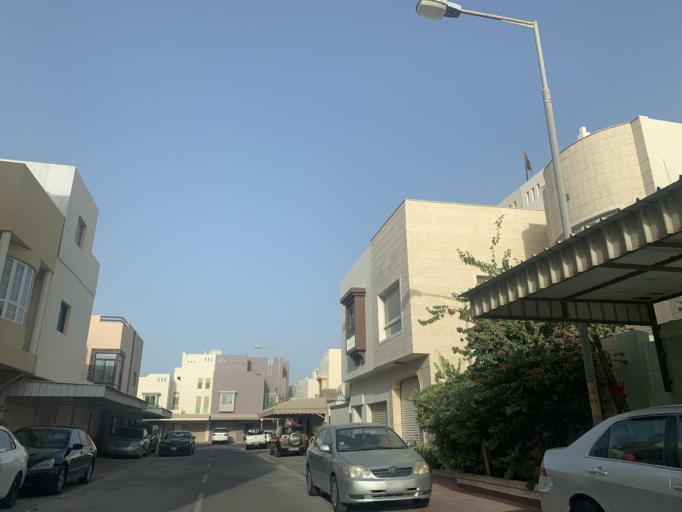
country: BH
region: Manama
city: Jidd Hafs
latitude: 26.2222
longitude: 50.5487
